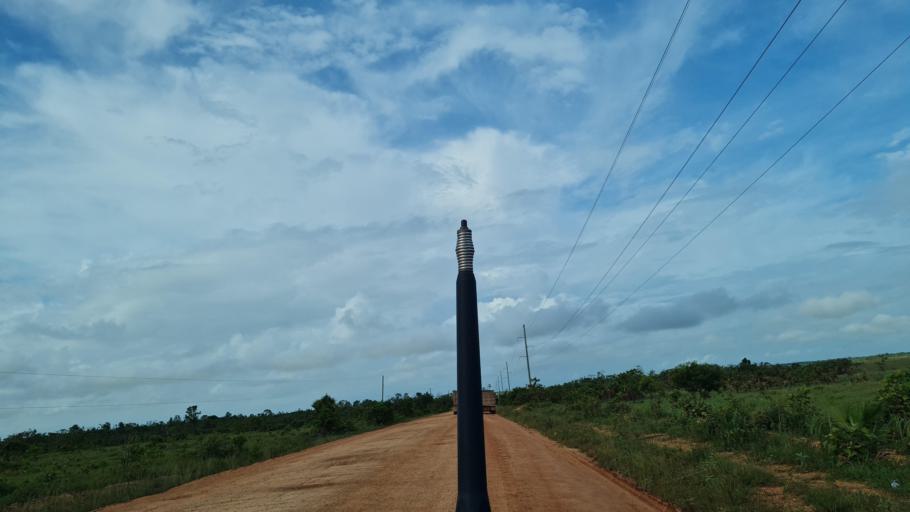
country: NI
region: Atlantico Norte (RAAN)
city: Puerto Cabezas
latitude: 14.1495
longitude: -83.5331
